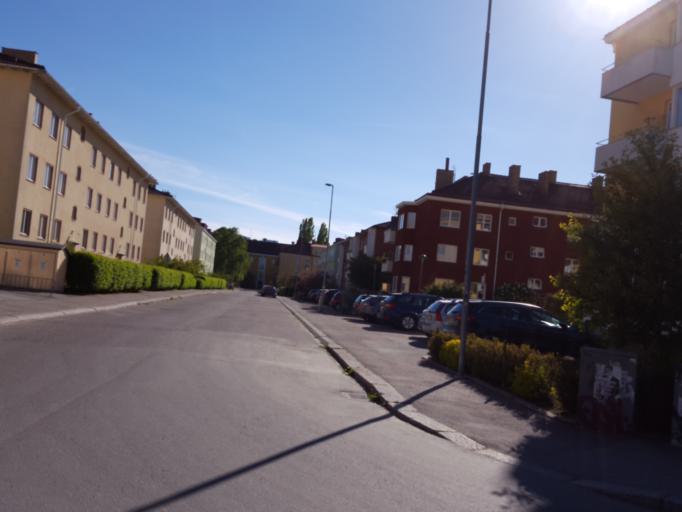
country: SE
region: Uppsala
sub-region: Uppsala Kommun
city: Uppsala
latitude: 59.8636
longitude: 17.6528
